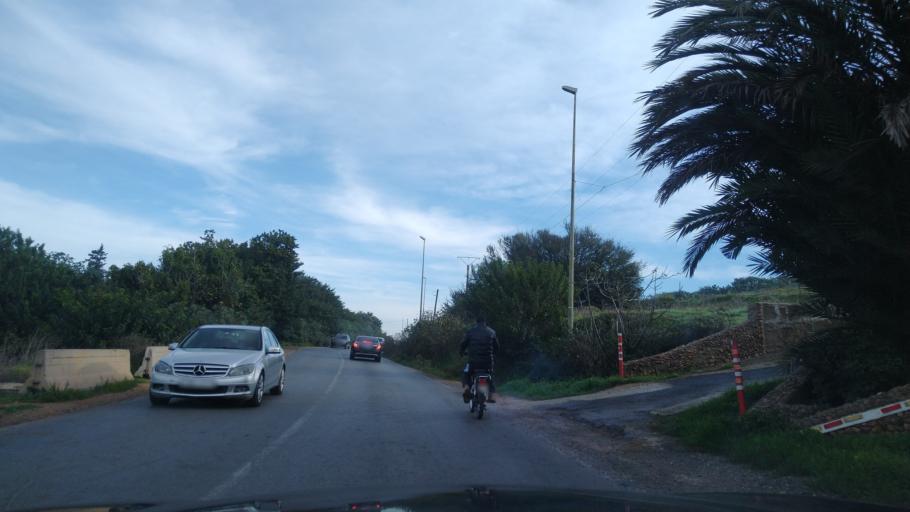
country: MA
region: Rabat-Sale-Zemmour-Zaer
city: Sale
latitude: 33.9965
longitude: -6.7548
